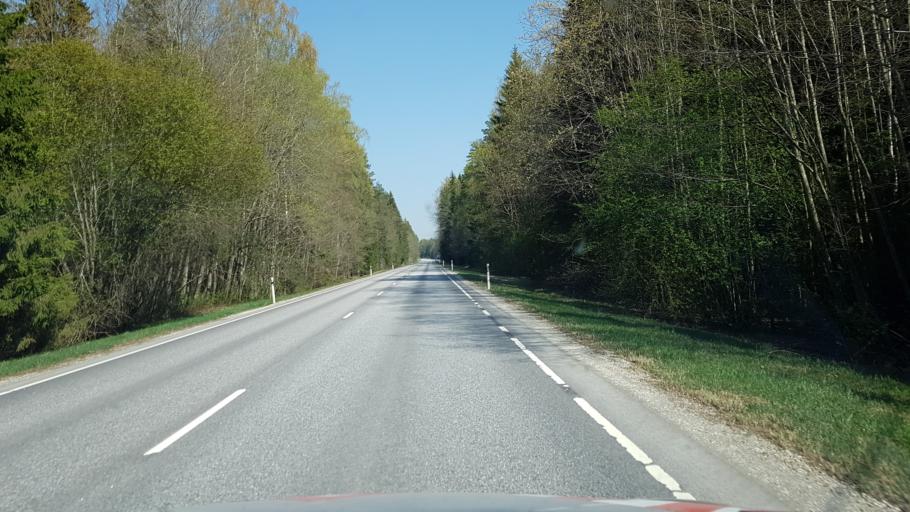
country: EE
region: Jaervamaa
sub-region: Tueri vald
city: Sarevere
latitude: 58.6918
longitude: 25.2489
